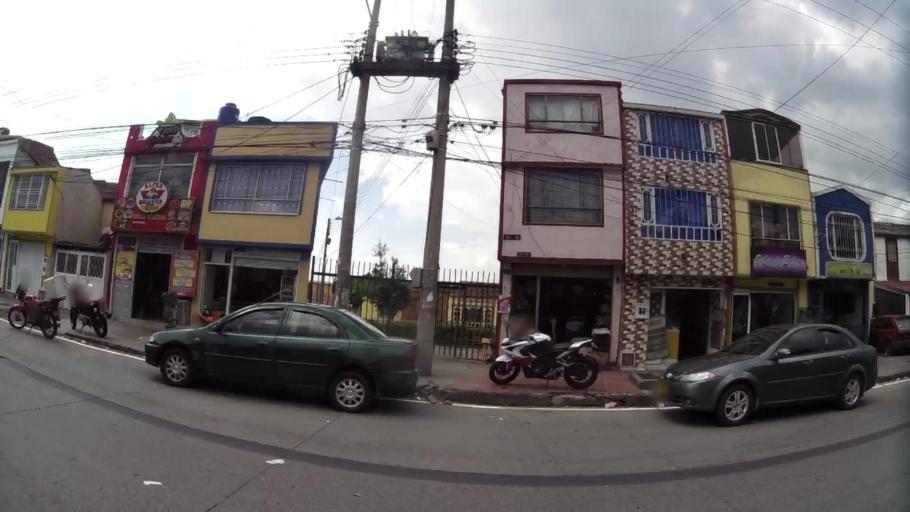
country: CO
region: Bogota D.C.
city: Bogota
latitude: 4.5622
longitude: -74.0973
